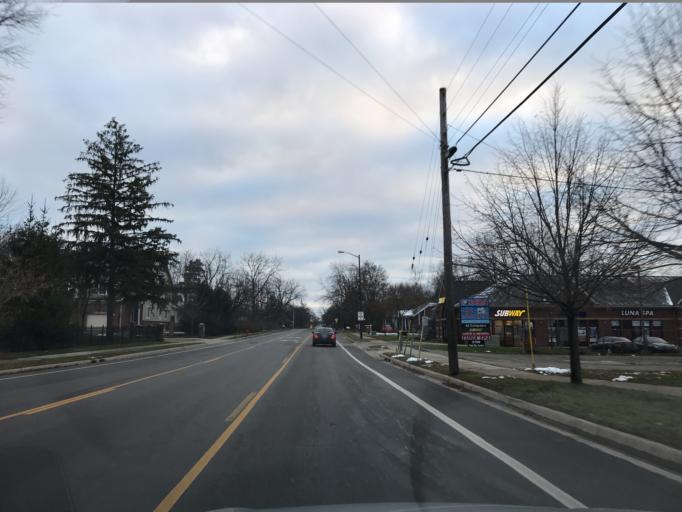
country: US
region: Michigan
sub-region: Washtenaw County
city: Ann Arbor
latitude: 42.2443
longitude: -83.7002
